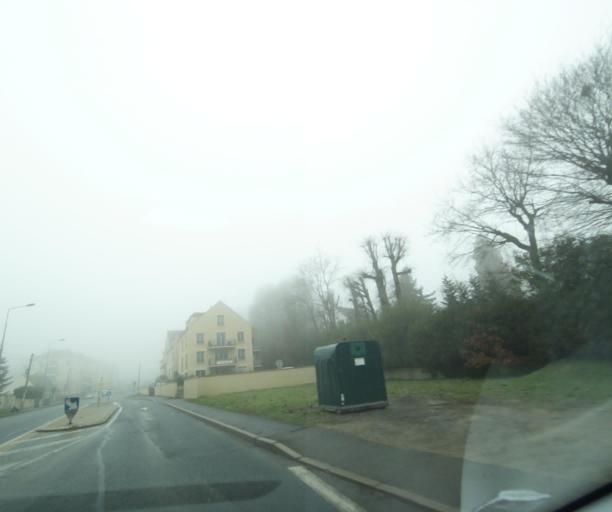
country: FR
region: Ile-de-France
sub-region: Departement de Seine-et-Marne
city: Dammartin-en-Goele
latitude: 49.0548
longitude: 2.6948
